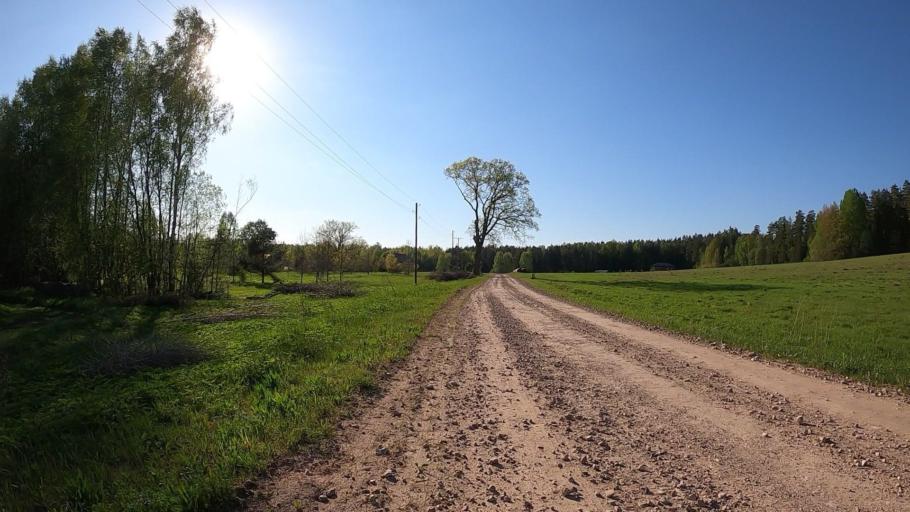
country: LV
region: Baldone
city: Baldone
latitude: 56.7629
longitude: 24.3753
